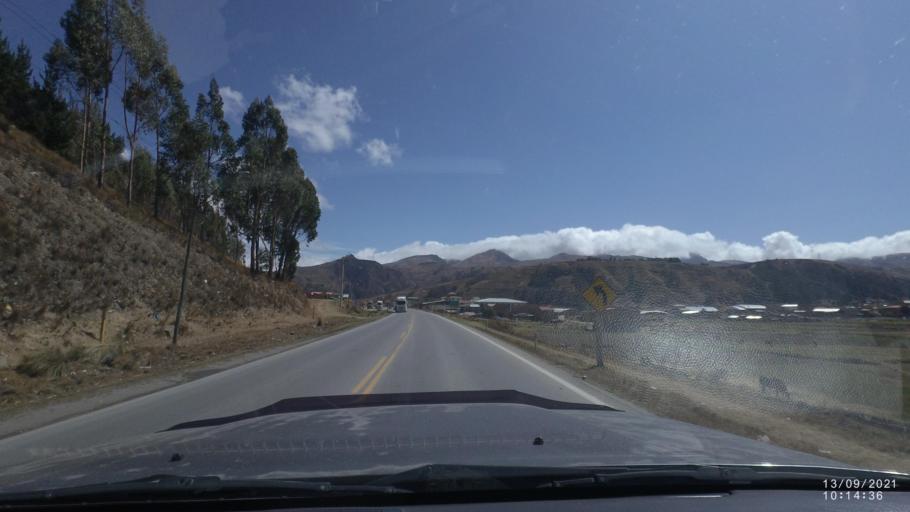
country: BO
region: Cochabamba
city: Colomi
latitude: -17.3756
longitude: -65.8342
